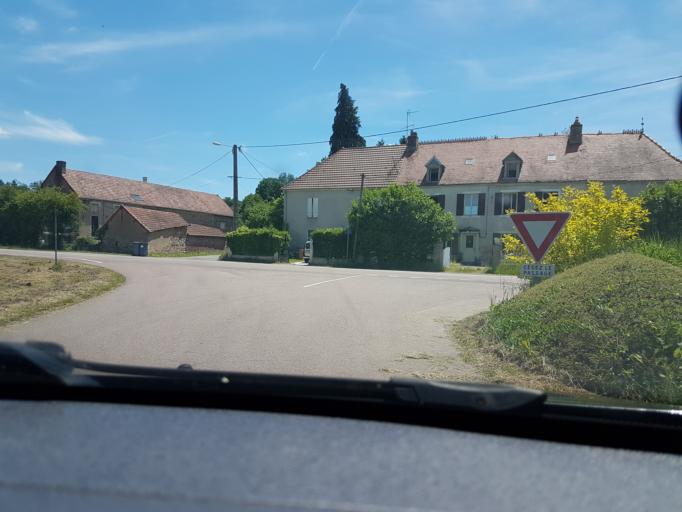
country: FR
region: Bourgogne
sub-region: Departement de Saone-et-Loire
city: Epinac
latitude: 46.9733
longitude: 4.5062
